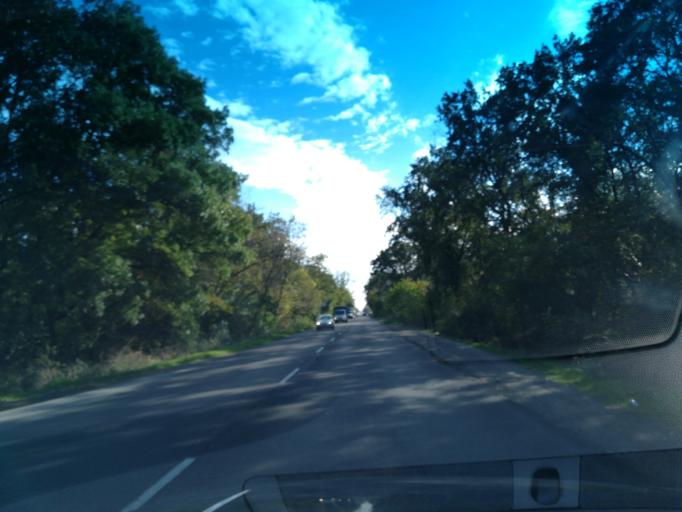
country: BG
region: Stara Zagora
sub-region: Obshtina Stara Zagora
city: Stara Zagora
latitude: 42.3530
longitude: 25.6580
